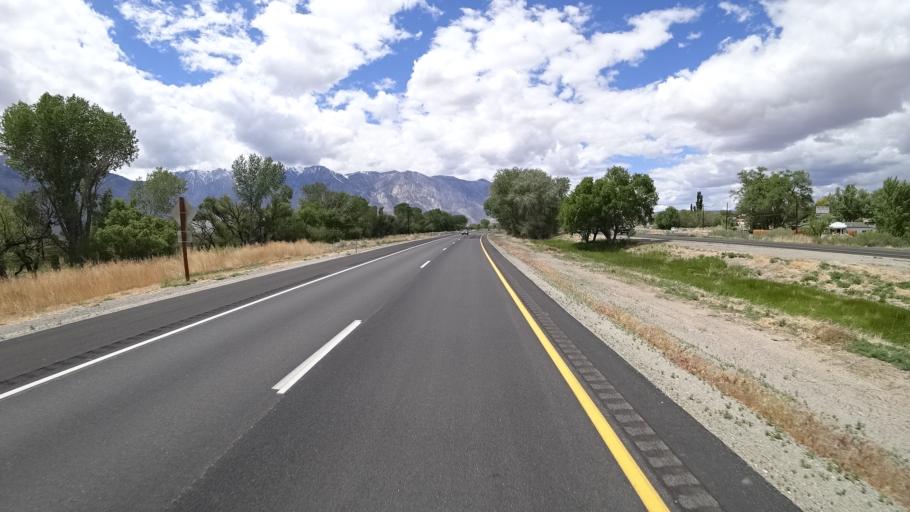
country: US
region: California
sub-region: Inyo County
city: West Bishop
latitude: 37.4066
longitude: -118.5456
